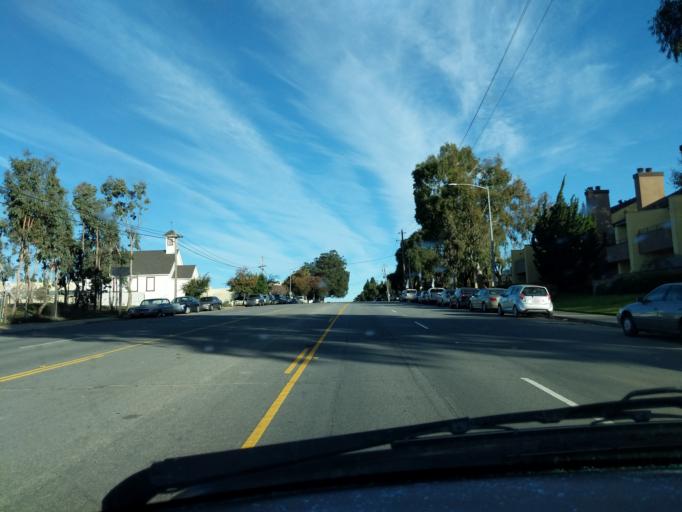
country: US
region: California
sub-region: Monterey County
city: Boronda
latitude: 36.7275
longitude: -121.6562
